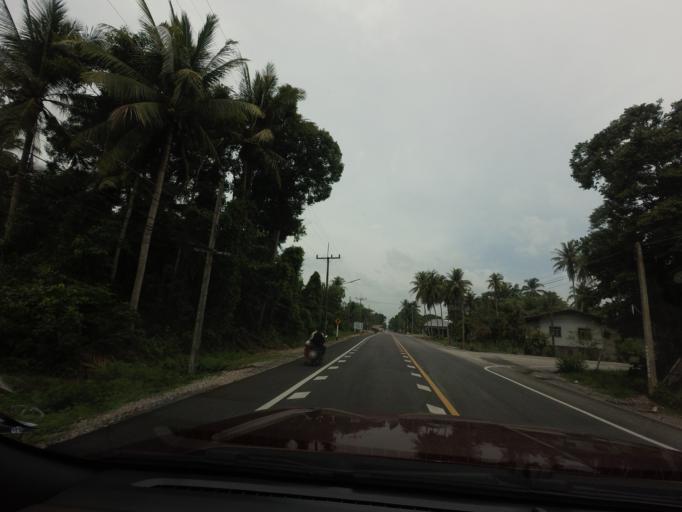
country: TH
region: Pattani
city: Yaring
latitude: 6.8588
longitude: 101.3635
